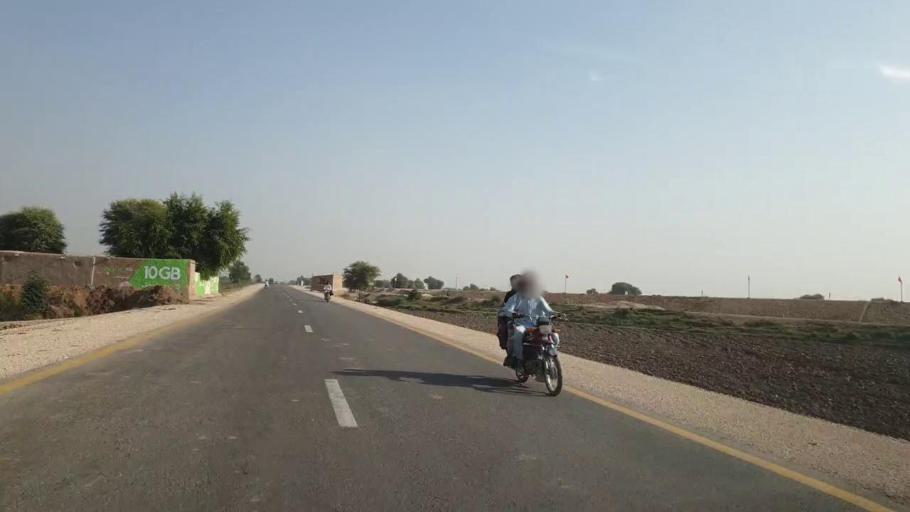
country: PK
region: Sindh
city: Sehwan
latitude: 26.4562
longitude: 67.8072
